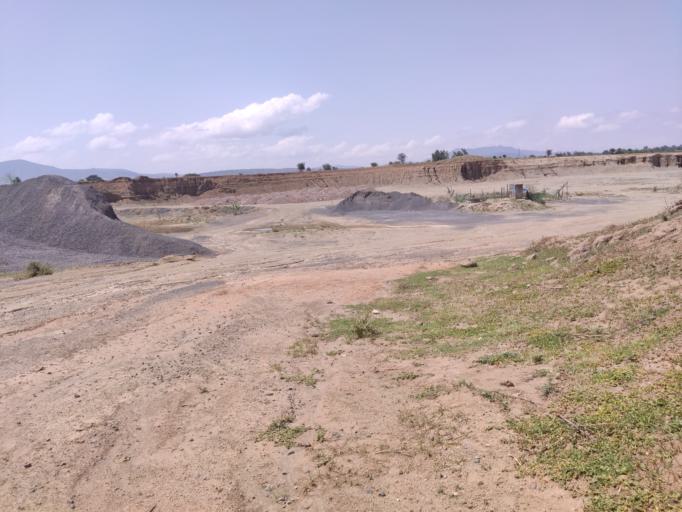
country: ET
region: Oromiya
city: Mojo
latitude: 8.3150
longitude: 38.9516
